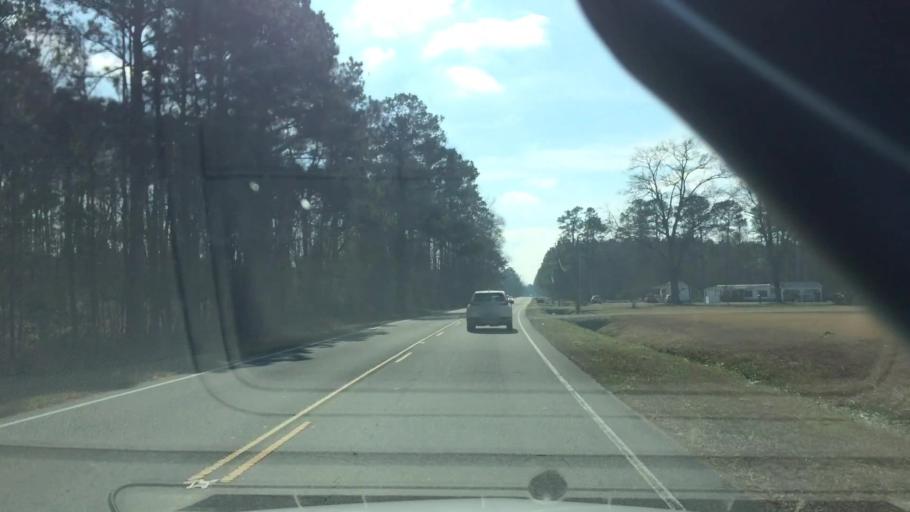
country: US
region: North Carolina
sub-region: Duplin County
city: Beulaville
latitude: 34.8689
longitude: -77.7923
